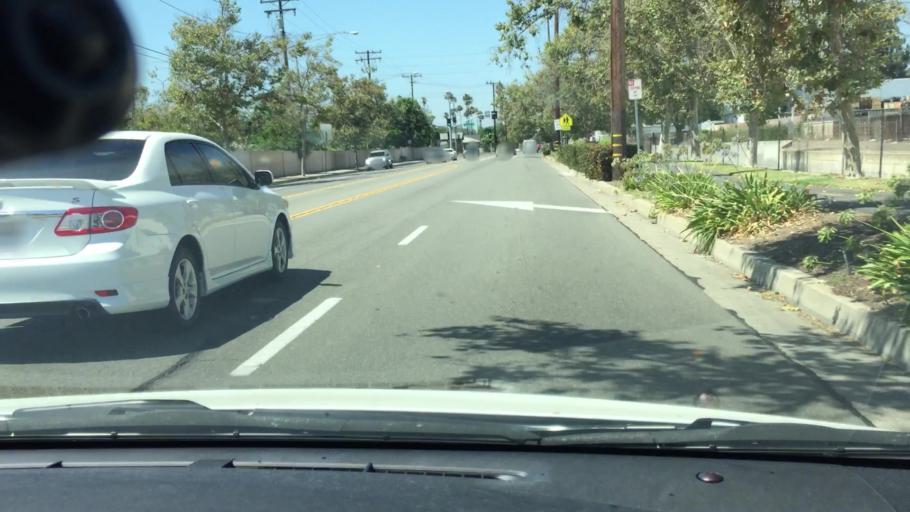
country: US
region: California
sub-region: Orange County
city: Santa Ana
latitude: 33.7146
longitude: -117.8767
